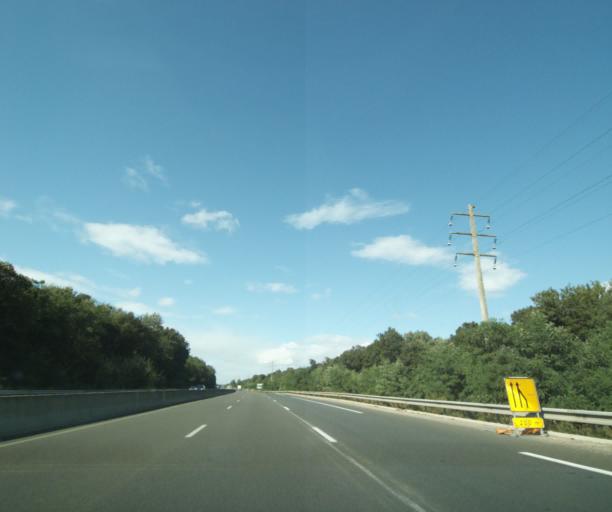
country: FR
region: Centre
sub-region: Departement du Loiret
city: Saint-Pryve-Saint-Mesmin
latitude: 47.8491
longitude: 1.8666
